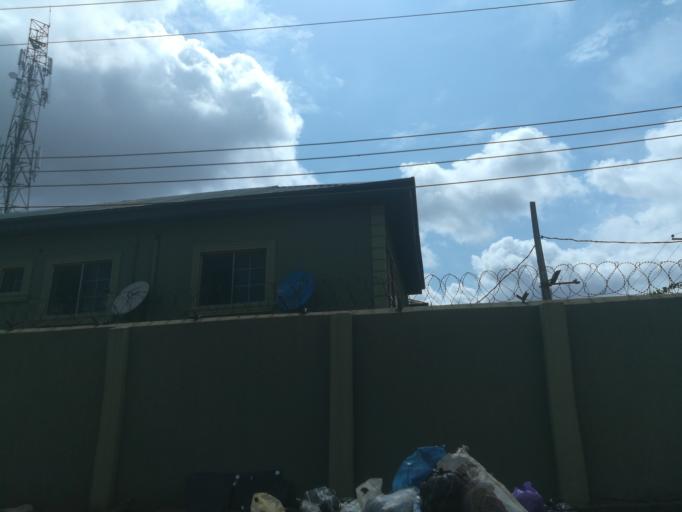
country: NG
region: Lagos
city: Somolu
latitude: 6.5296
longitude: 3.3805
